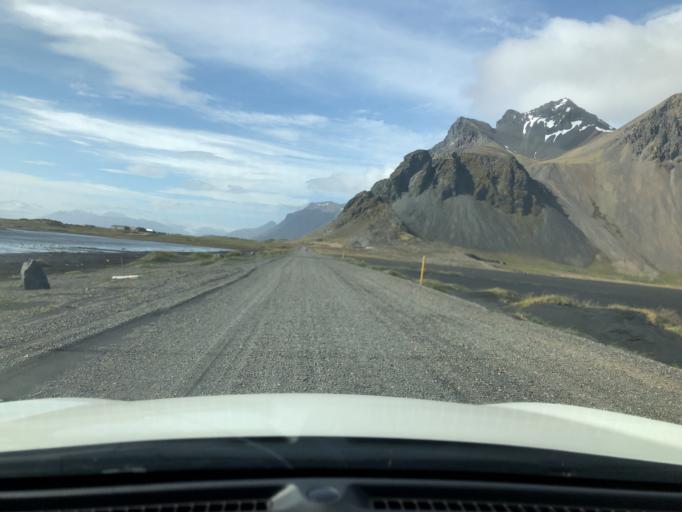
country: IS
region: East
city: Hoefn
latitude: 64.2493
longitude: -14.9830
